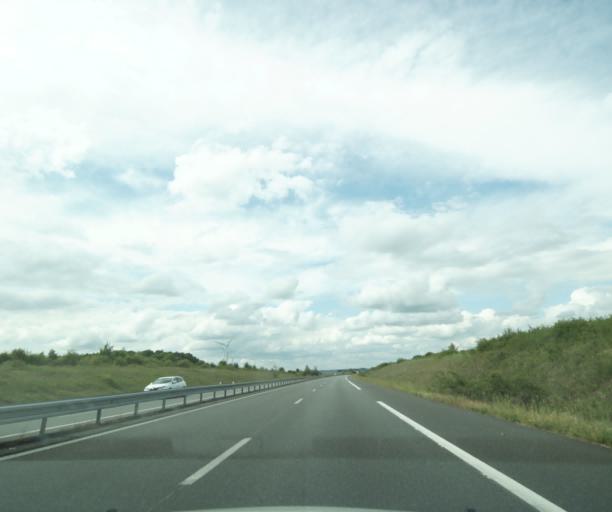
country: FR
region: Centre
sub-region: Departement du Cher
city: Mehun-sur-Yevre
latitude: 47.1296
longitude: 2.1889
